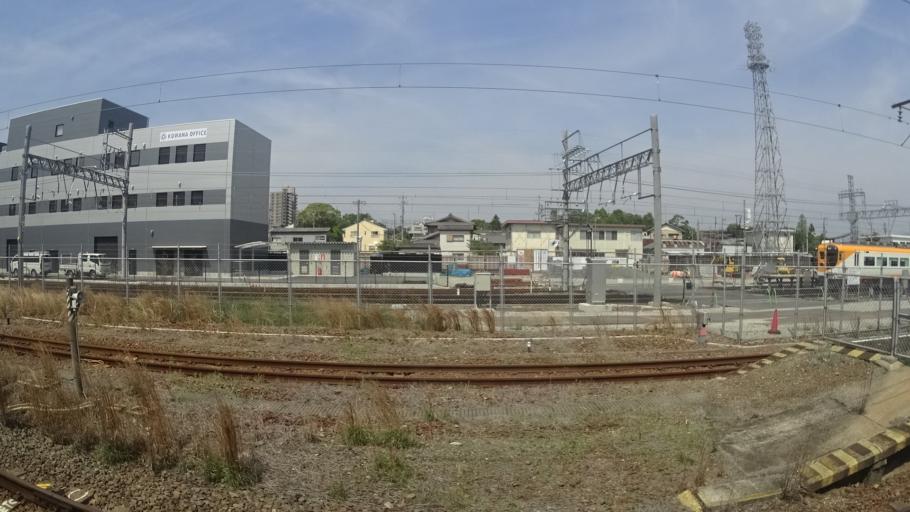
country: JP
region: Aichi
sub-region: Tsushima-shi
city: Tsushima
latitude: 35.0652
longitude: 136.6835
